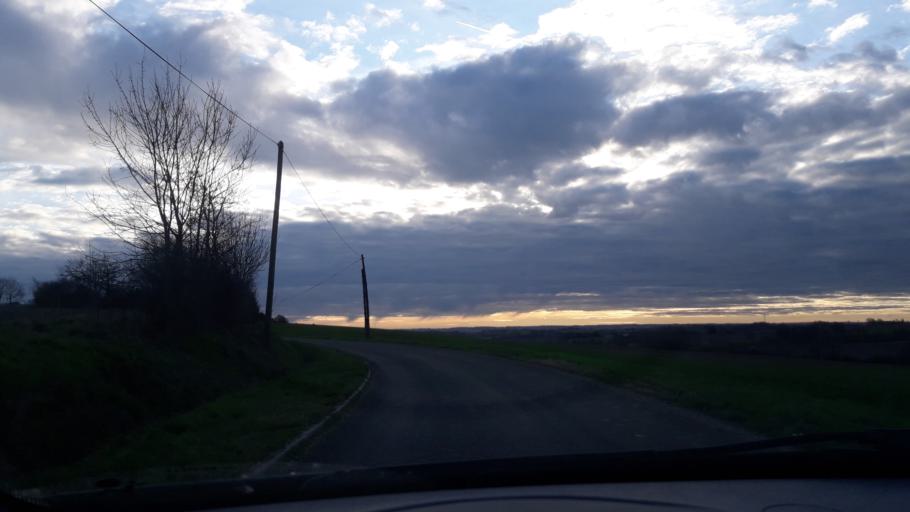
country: FR
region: Midi-Pyrenees
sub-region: Departement du Gers
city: Pujaudran
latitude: 43.6692
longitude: 1.0318
